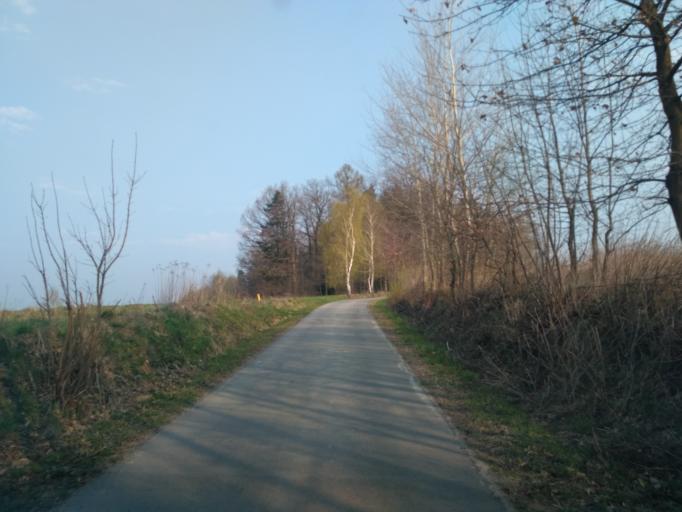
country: PL
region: Subcarpathian Voivodeship
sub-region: Powiat strzyzowski
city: Wisniowa
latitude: 49.8796
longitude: 21.6360
